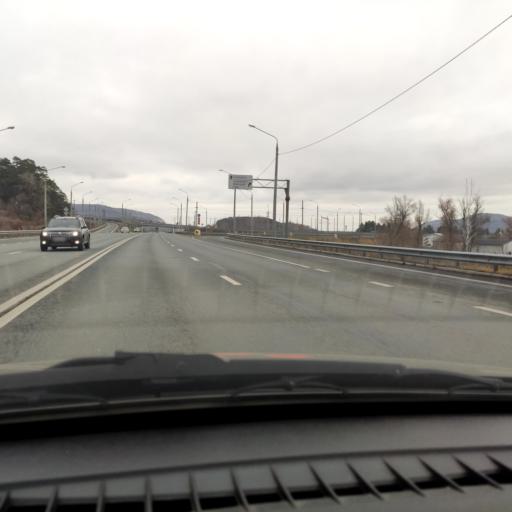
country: RU
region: Samara
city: Volzhskiy
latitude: 53.4373
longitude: 50.1117
